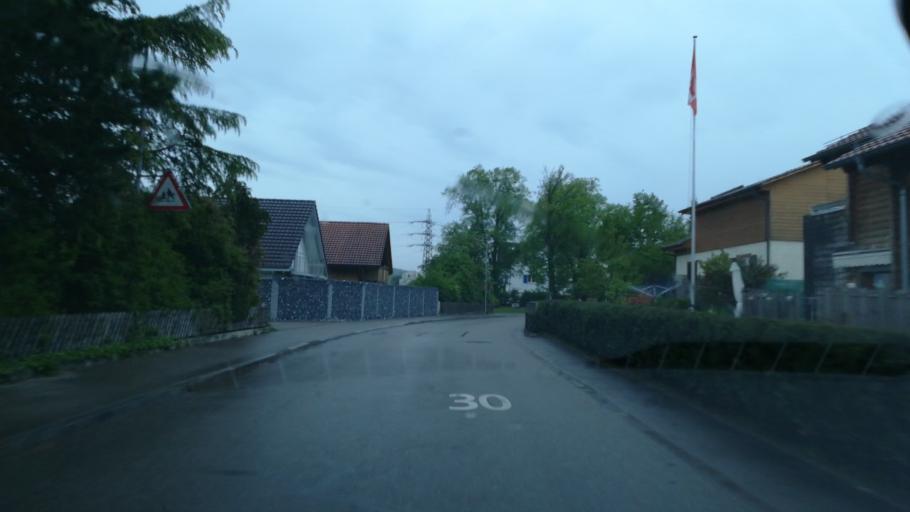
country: CH
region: Zurich
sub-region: Bezirk Buelach
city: Glattfelden
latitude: 47.5712
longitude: 8.4715
